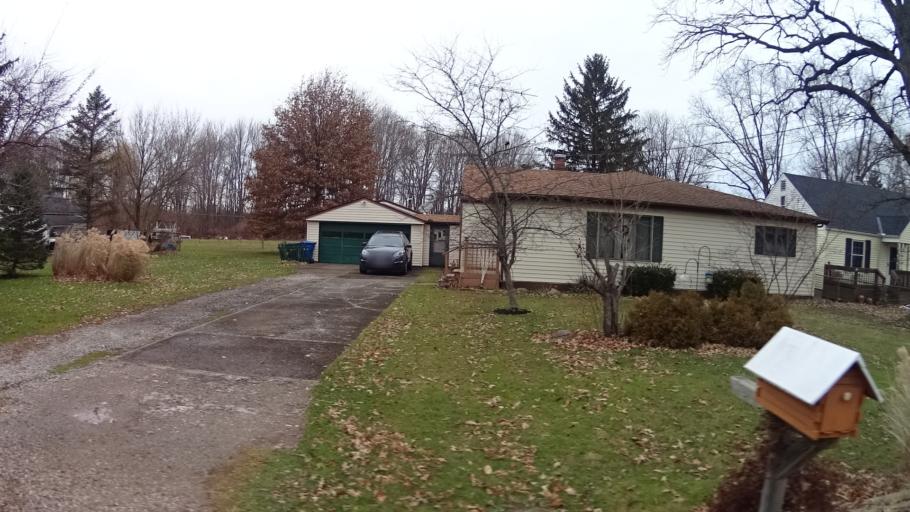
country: US
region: Ohio
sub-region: Lorain County
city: North Ridgeville
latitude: 41.3636
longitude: -82.0207
